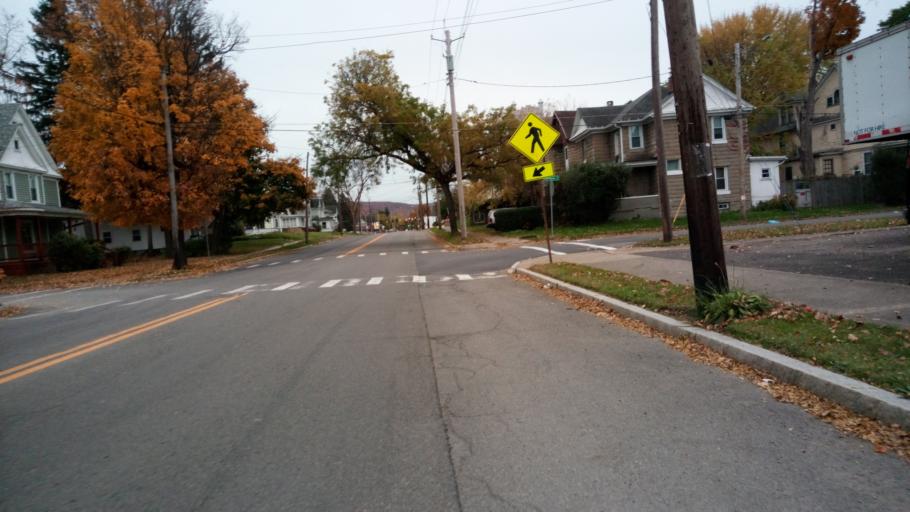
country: US
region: New York
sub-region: Chemung County
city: Elmira
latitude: 42.0806
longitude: -76.8022
